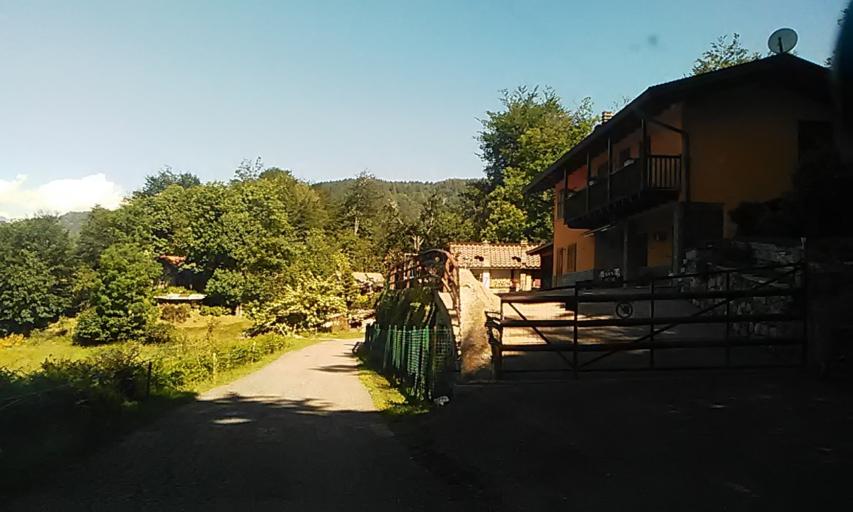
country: IT
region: Piedmont
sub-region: Provincia di Vercelli
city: Civiasco
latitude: 45.8392
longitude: 8.2996
